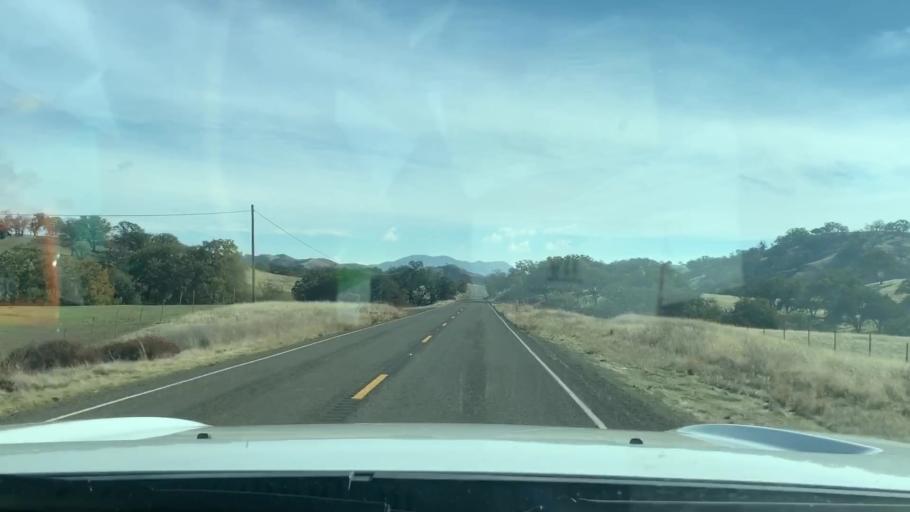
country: US
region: California
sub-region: Fresno County
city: Coalinga
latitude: 36.0987
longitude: -120.5342
